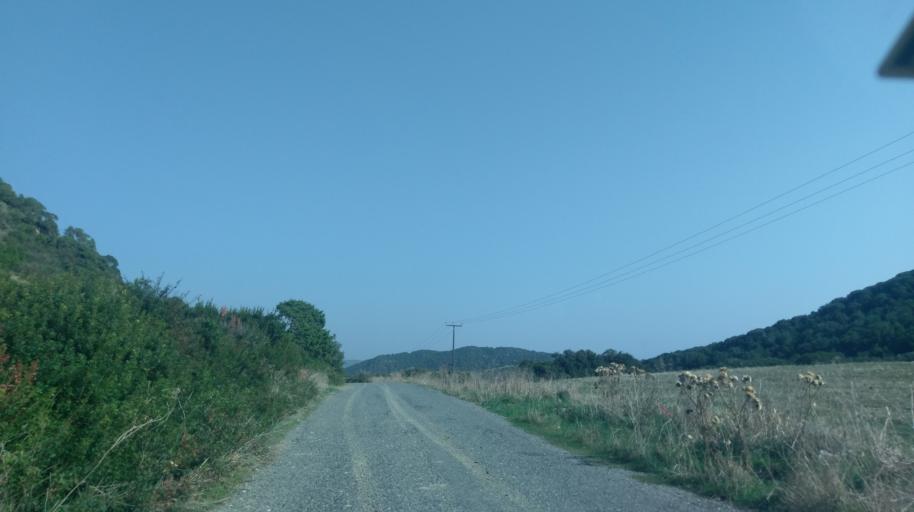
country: CY
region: Ammochostos
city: Rizokarpaso
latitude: 35.6335
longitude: 34.5028
